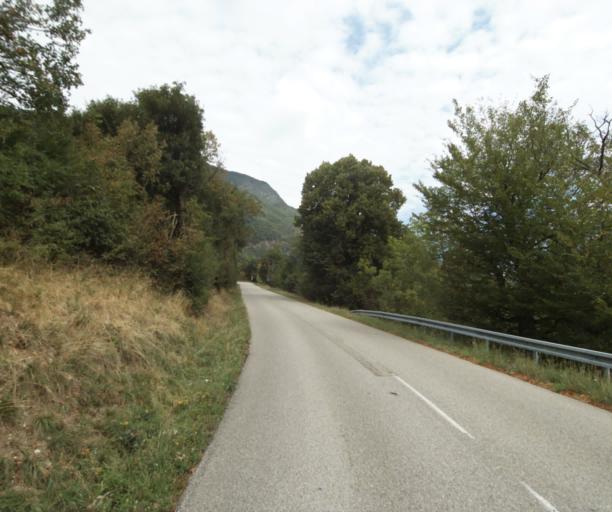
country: FR
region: Rhone-Alpes
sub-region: Departement de l'Isere
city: Saint-Egreve
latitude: 45.2492
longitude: 5.6966
